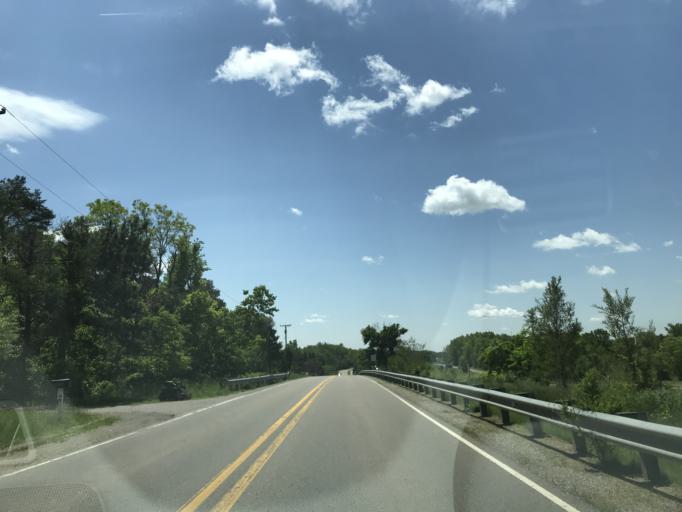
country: US
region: Michigan
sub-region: Livingston County
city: Whitmore Lake
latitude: 42.4836
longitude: -83.7562
